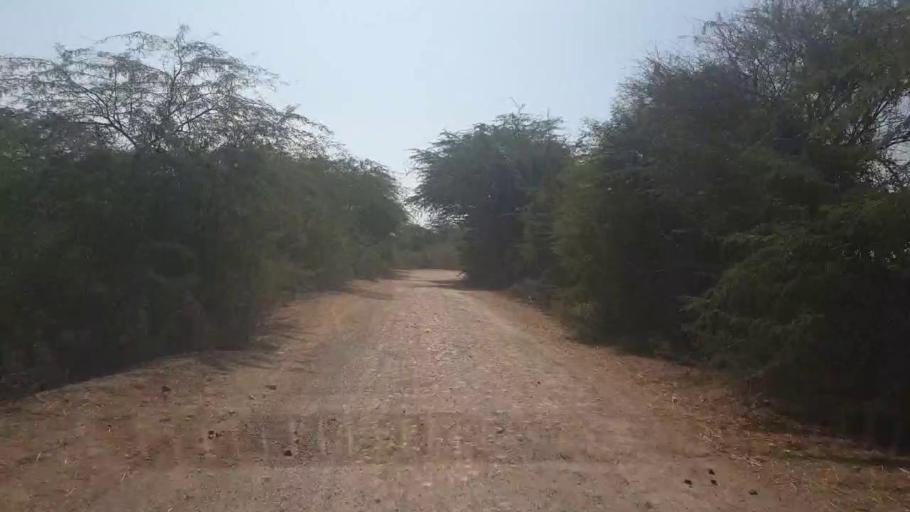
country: PK
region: Sindh
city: Badin
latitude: 24.6005
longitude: 68.8541
